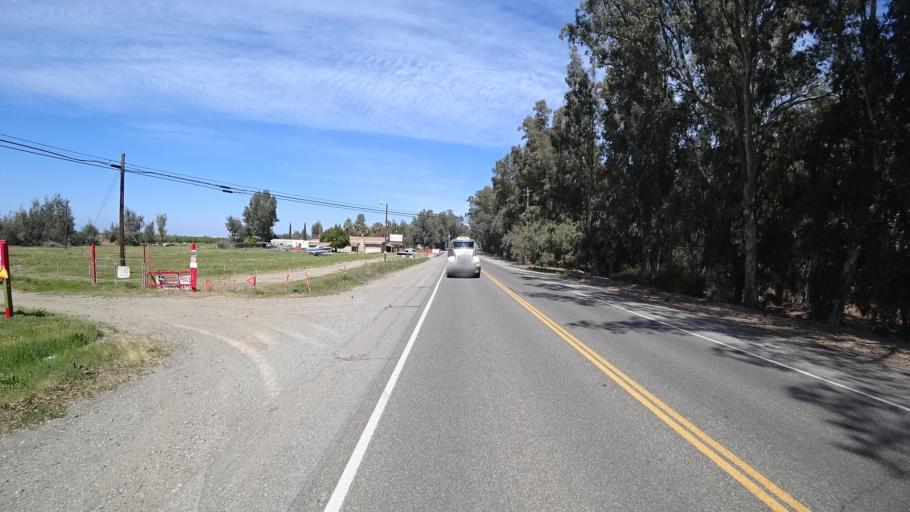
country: US
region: California
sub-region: Glenn County
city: Willows
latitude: 39.5923
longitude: -122.1948
